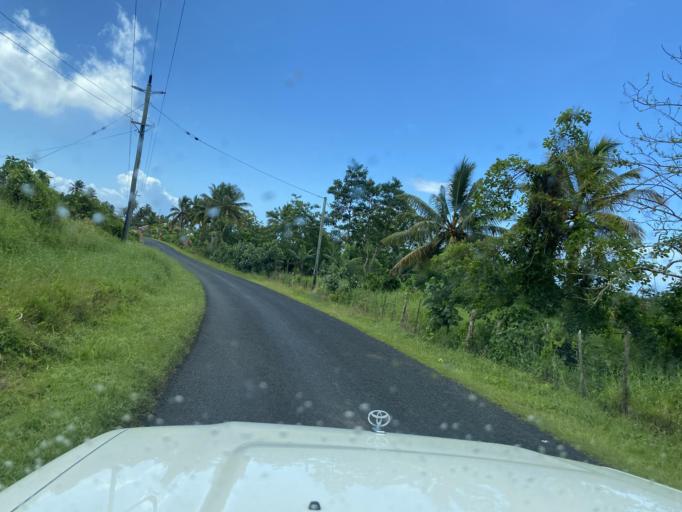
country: WS
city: Matavai
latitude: -13.9876
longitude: -171.5876
